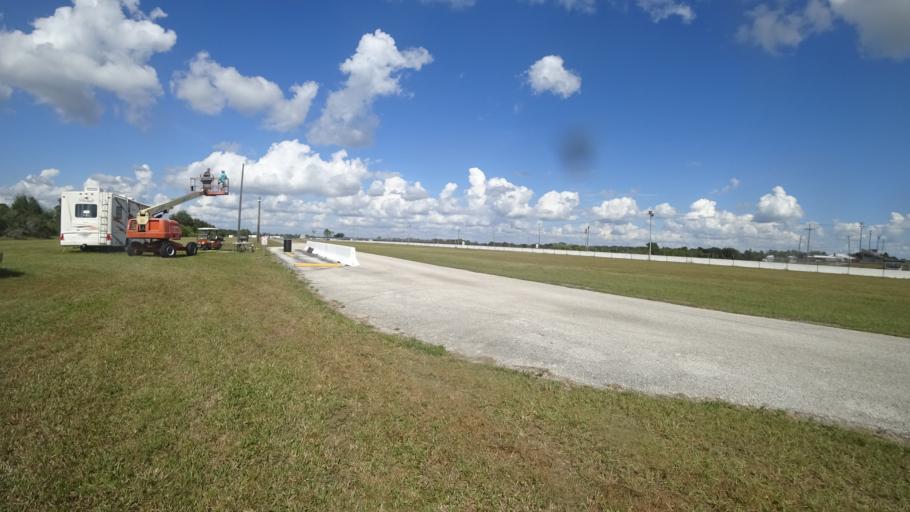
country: US
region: Florida
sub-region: Sarasota County
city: The Meadows
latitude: 27.4660
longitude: -82.3275
